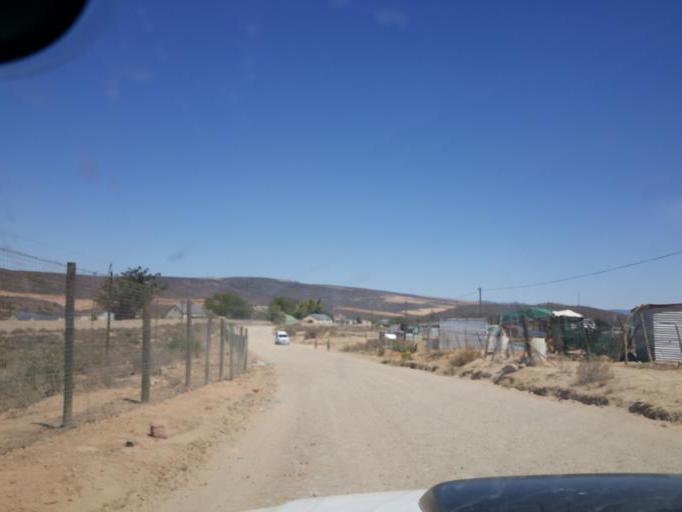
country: ZA
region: Western Cape
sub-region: West Coast District Municipality
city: Clanwilliam
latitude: -32.1952
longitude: 18.8925
